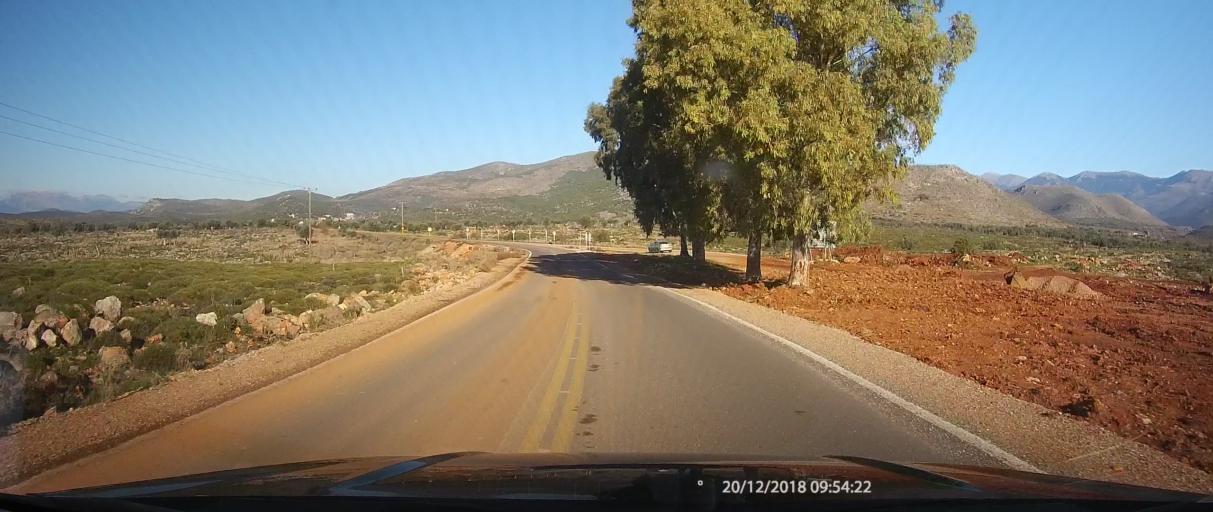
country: GR
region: Peloponnese
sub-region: Nomos Lakonias
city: Yerakion
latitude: 37.0159
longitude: 22.6354
